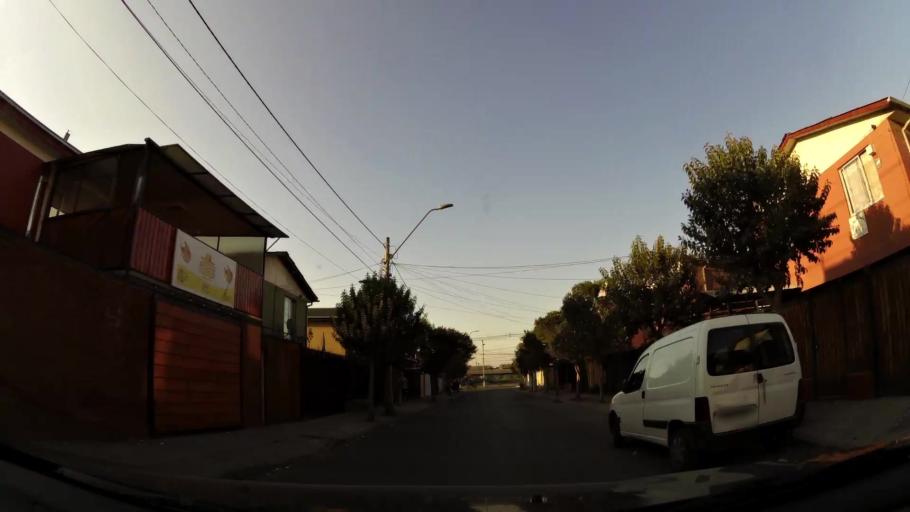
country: CL
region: Santiago Metropolitan
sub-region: Provincia de Maipo
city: San Bernardo
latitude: -33.5963
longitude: -70.6716
